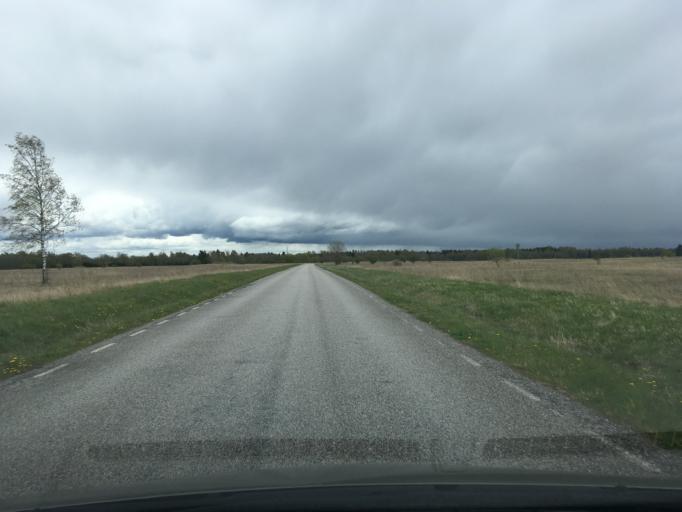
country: EE
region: Harju
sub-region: Rae vald
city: Vaida
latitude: 59.3558
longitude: 24.9821
